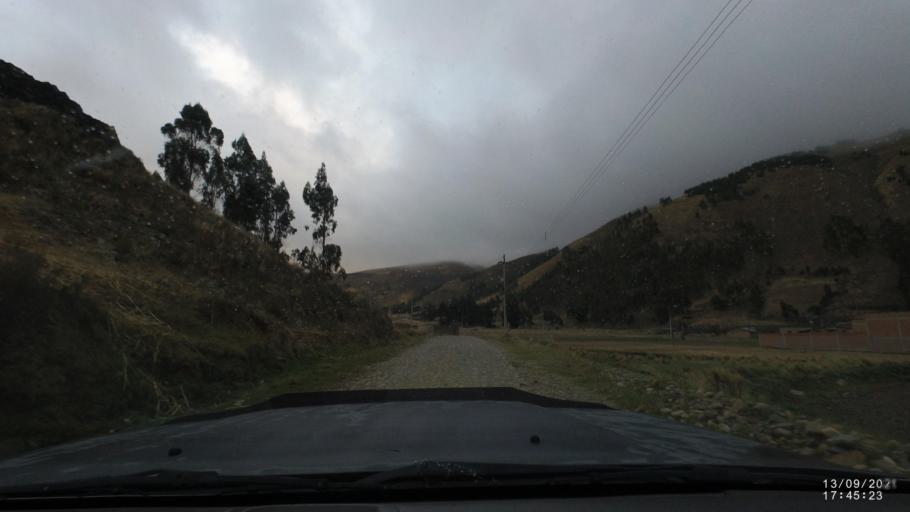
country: BO
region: Cochabamba
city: Colomi
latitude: -17.3774
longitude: -65.8324
